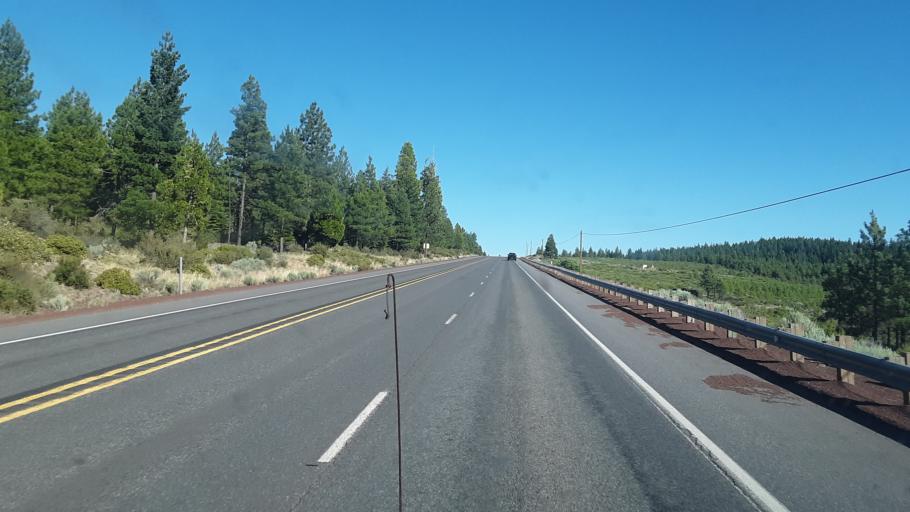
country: US
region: Oregon
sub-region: Klamath County
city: Klamath Falls
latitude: 42.3567
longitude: -121.9883
